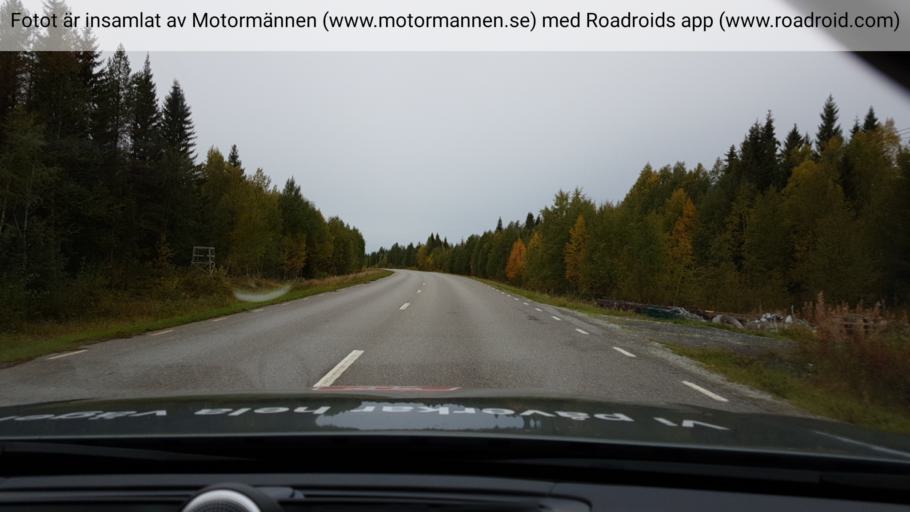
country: SE
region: Jaemtland
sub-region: Stroemsunds Kommun
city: Stroemsund
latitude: 64.3044
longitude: 15.3018
